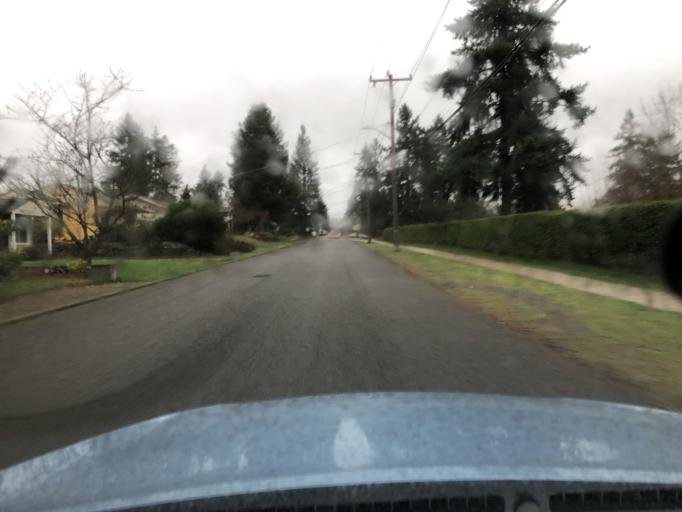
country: US
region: Washington
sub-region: King County
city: Lake Forest Park
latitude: 47.7398
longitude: -122.2993
